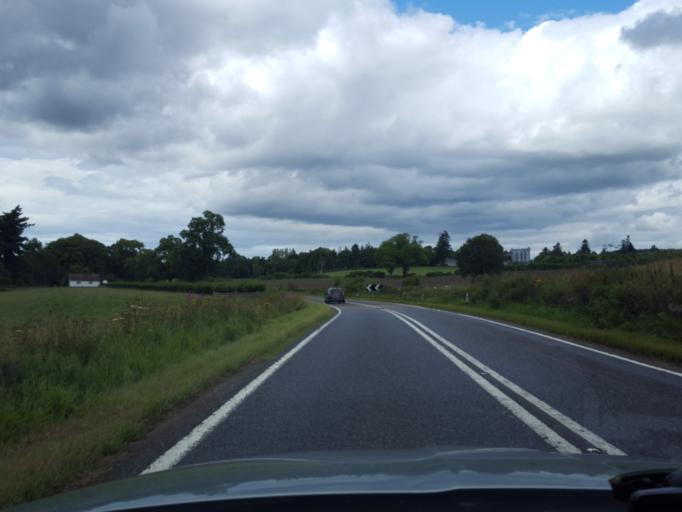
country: GB
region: Scotland
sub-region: Moray
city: Rothes
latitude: 57.4058
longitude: -3.3570
